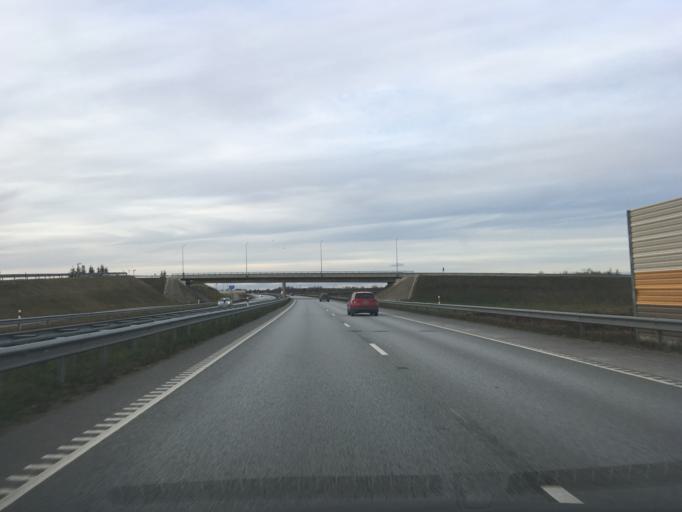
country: EE
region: Ida-Virumaa
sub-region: Johvi vald
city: Johvi
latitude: 59.3738
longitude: 27.3813
